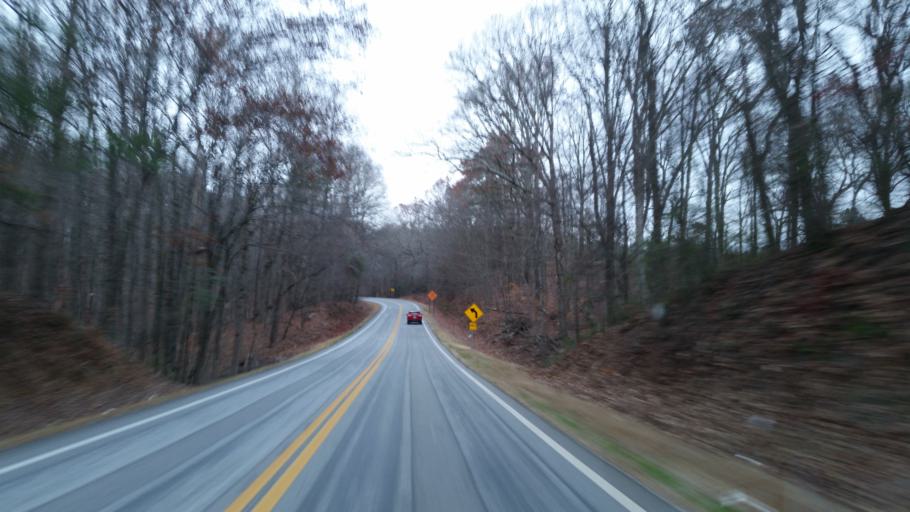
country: US
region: Georgia
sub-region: Dawson County
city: Dawsonville
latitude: 34.4152
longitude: -84.0293
